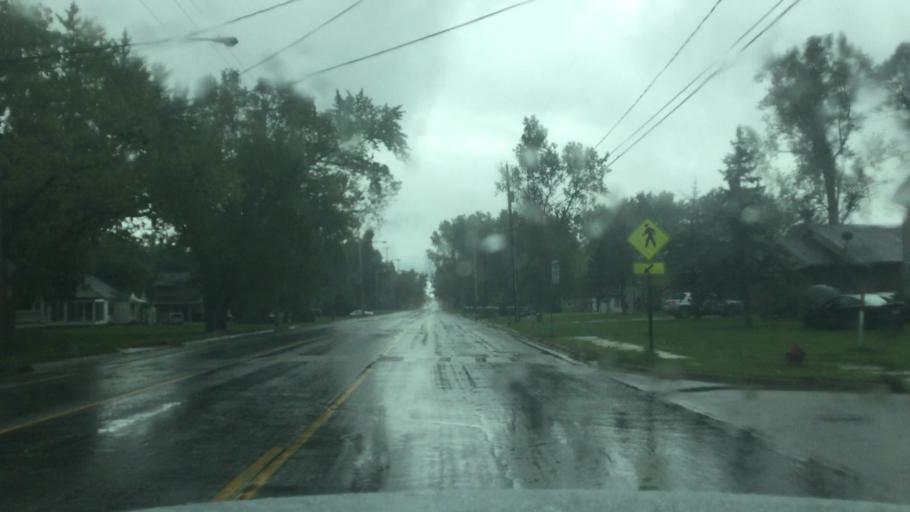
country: US
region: Michigan
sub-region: Eaton County
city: Dimondale
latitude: 42.6806
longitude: -84.6031
